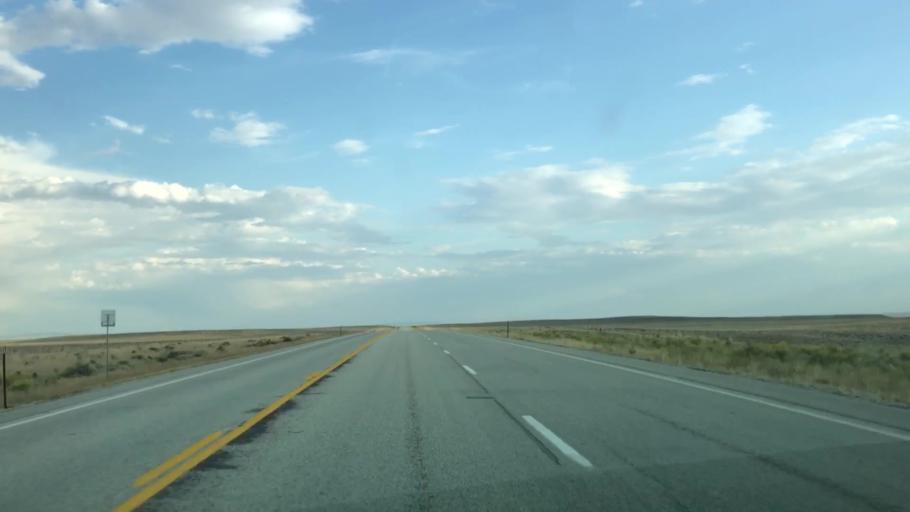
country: US
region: Wyoming
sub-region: Sweetwater County
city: North Rock Springs
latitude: 42.2760
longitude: -109.4825
